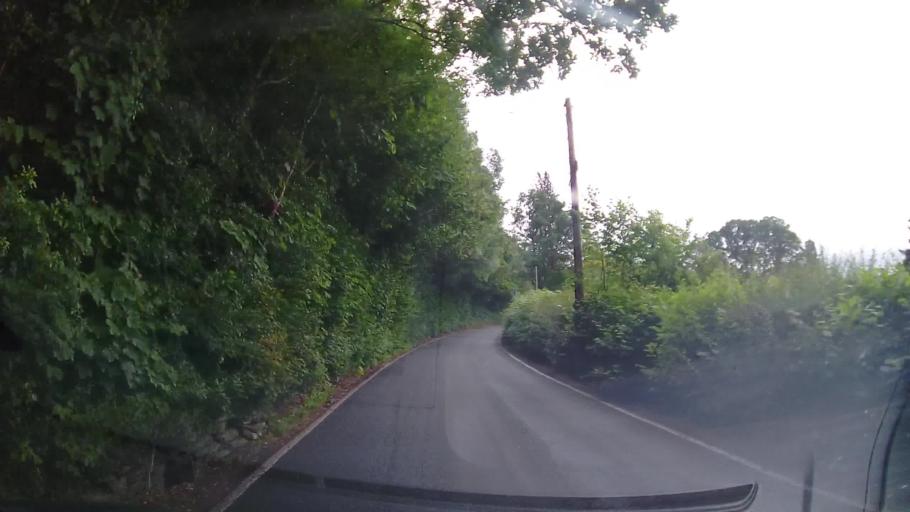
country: GB
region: Wales
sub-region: Conwy
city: Llangwm
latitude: 52.9164
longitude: -3.5118
